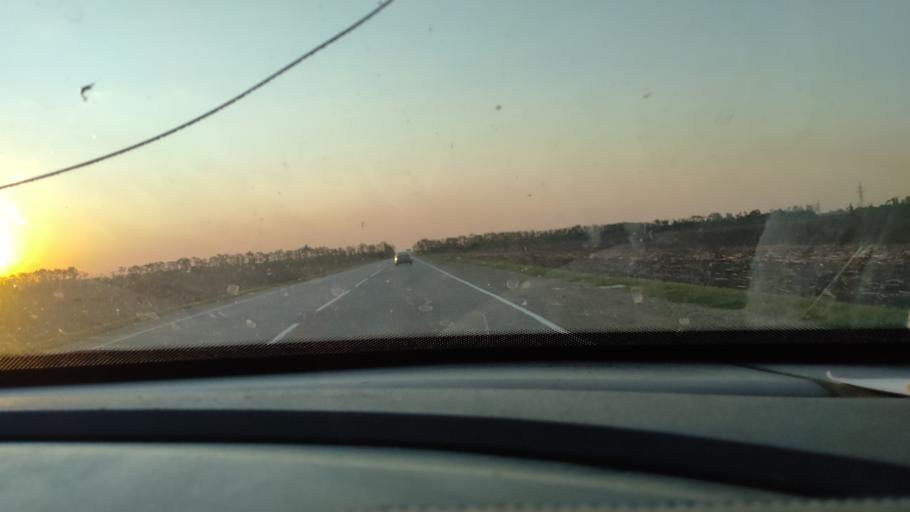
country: RU
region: Krasnodarskiy
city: Starominskaya
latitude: 46.4952
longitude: 39.0552
